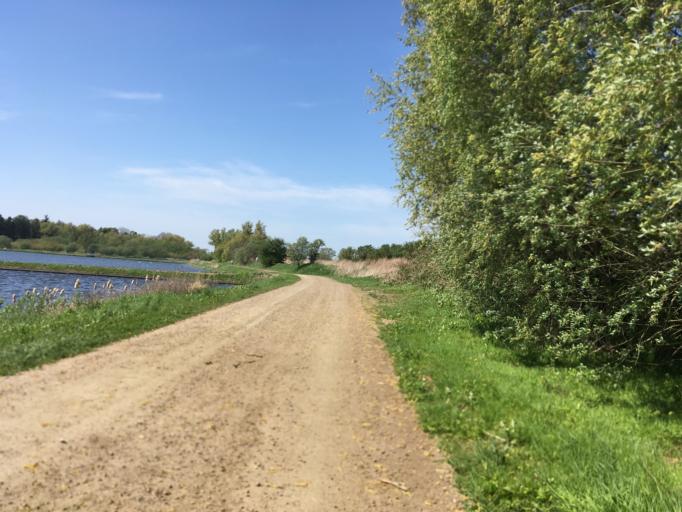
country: SE
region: Skane
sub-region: Staffanstorps Kommun
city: Hjaerup
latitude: 55.6994
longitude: 13.1555
